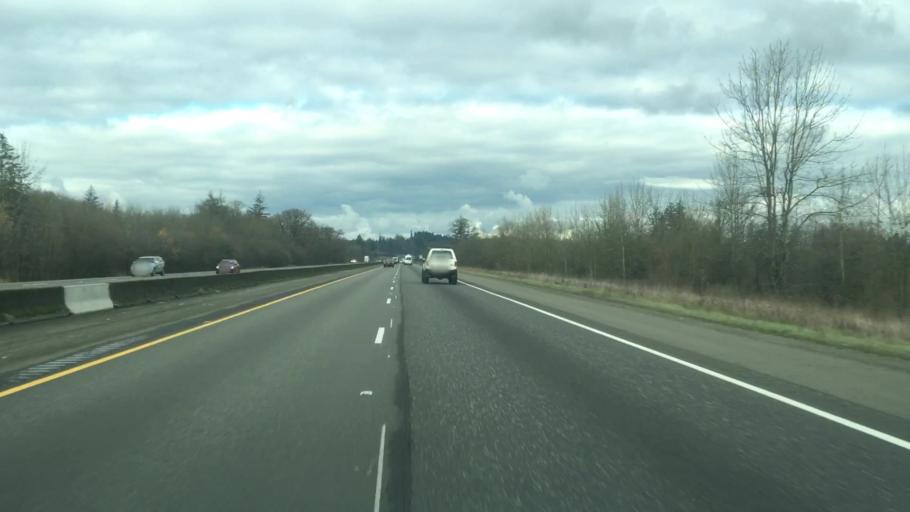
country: US
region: Washington
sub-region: Lewis County
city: Winlock
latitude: 46.4607
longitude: -122.8854
